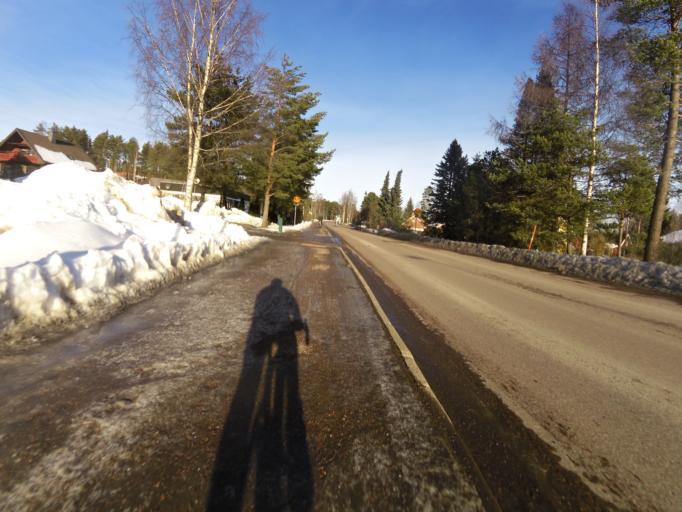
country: SE
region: Gaevleborg
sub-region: Gavle Kommun
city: Valbo
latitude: 60.6523
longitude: 17.0431
